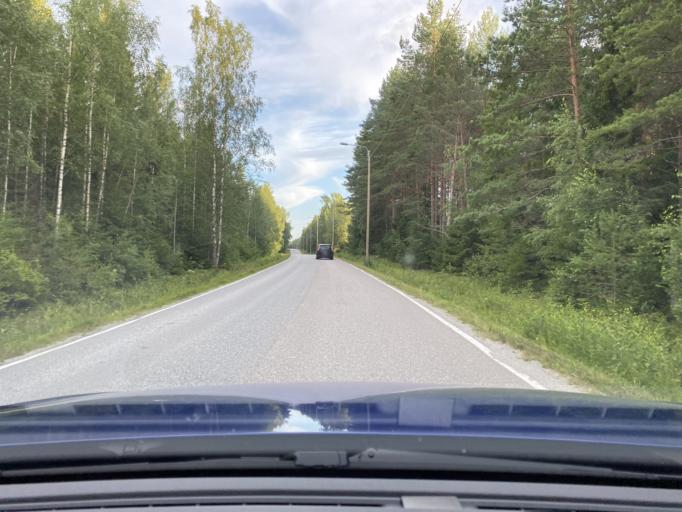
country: FI
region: Ostrobothnia
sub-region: Vaasa
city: Korsnaes
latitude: 62.9526
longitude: 21.1764
